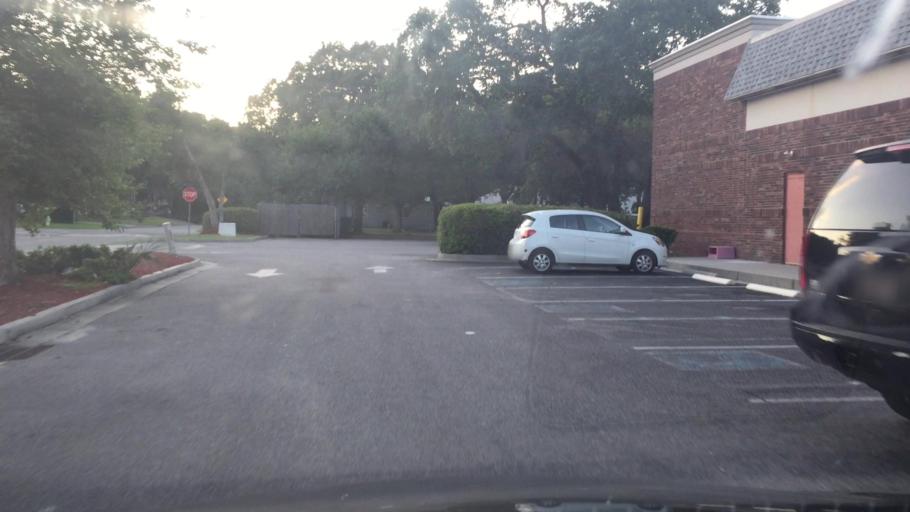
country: US
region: South Carolina
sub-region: Horry County
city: Myrtle Beach
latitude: 33.6822
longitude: -78.8957
